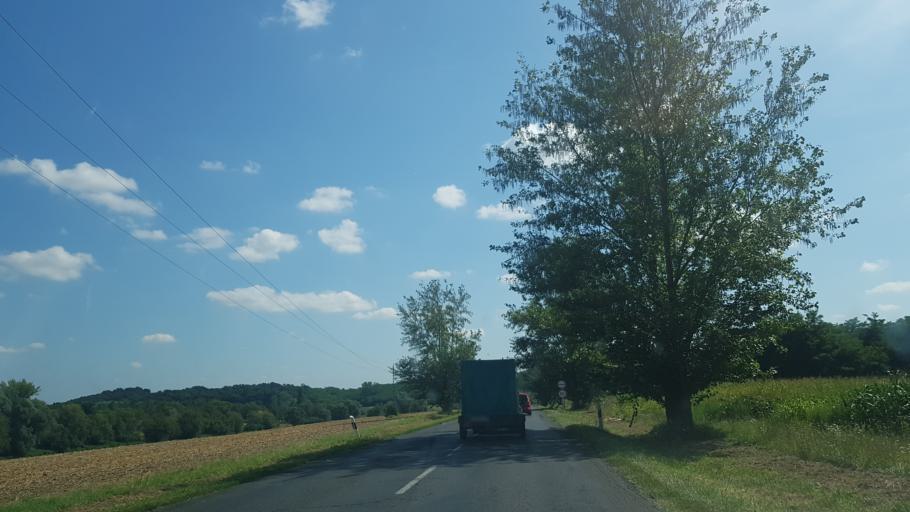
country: HU
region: Somogy
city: Bohonye
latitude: 46.4623
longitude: 17.3742
